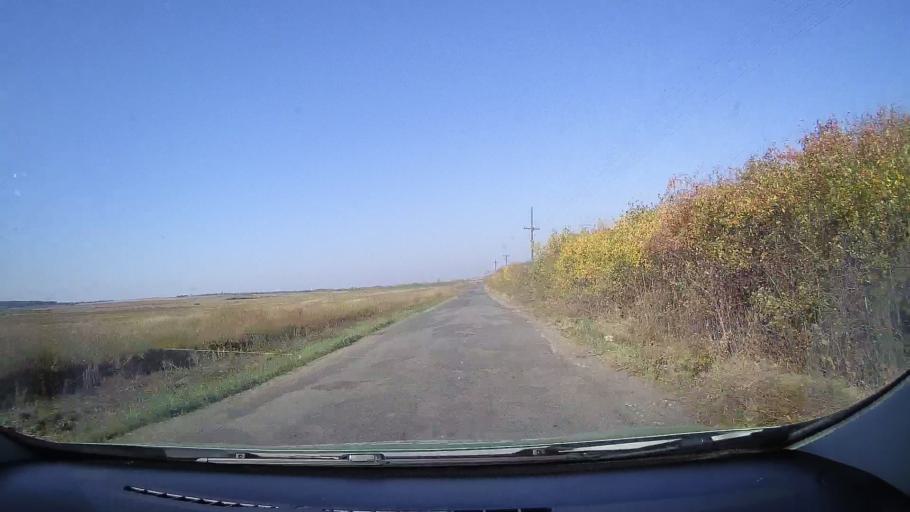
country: RO
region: Satu Mare
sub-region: Oras Tasnad
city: Tasnad
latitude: 47.4784
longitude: 22.5485
